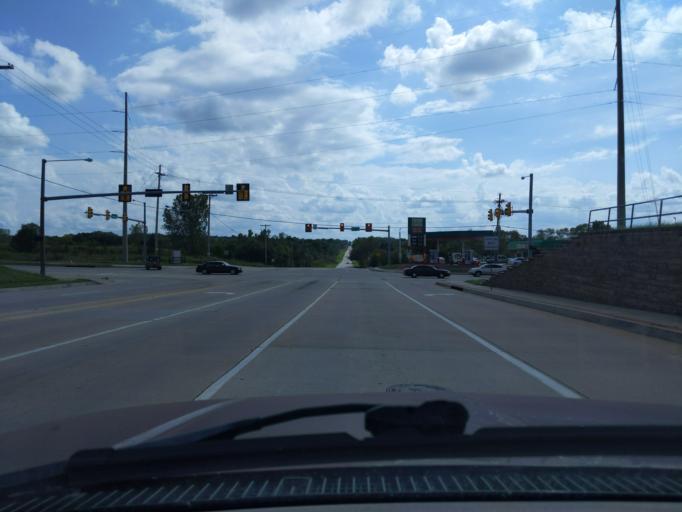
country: US
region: Oklahoma
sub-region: Tulsa County
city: Oakhurst
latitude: 36.0759
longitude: -96.0118
